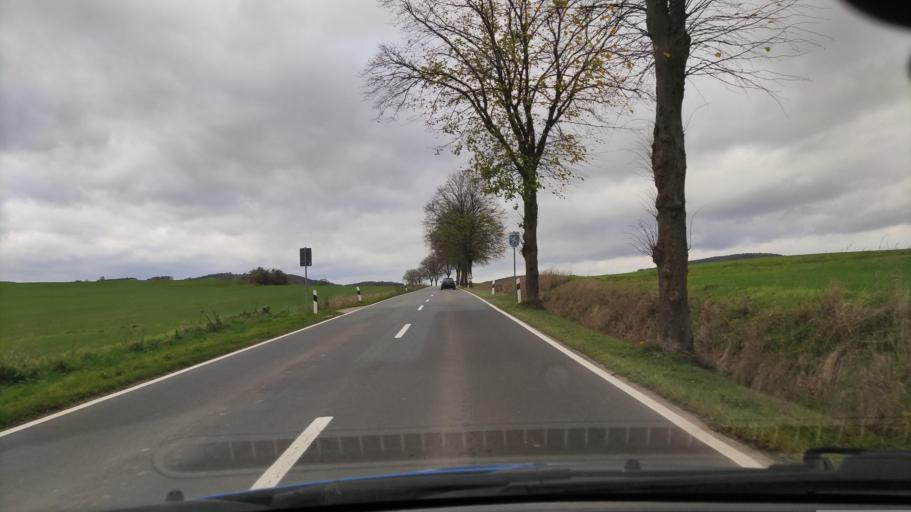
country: DE
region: Lower Saxony
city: Wangelnstedt
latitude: 51.8672
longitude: 9.7021
